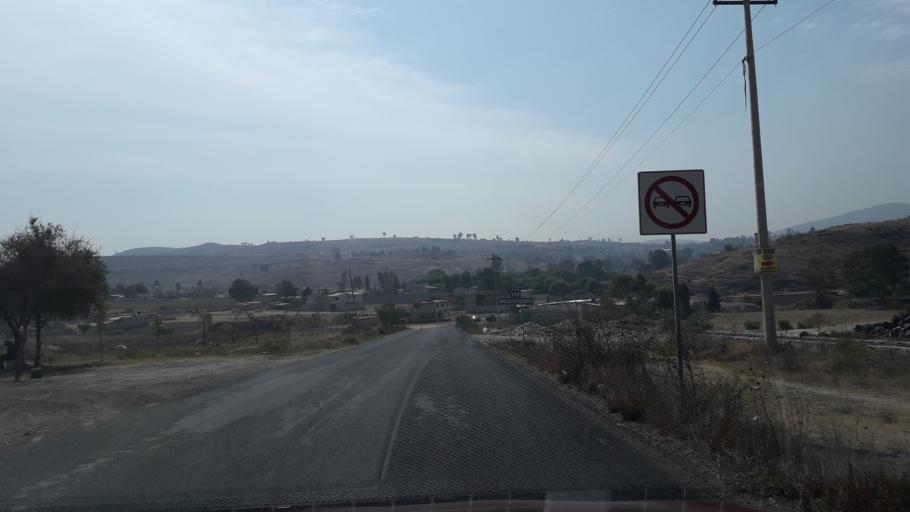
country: MX
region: Puebla
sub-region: Puebla
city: El Capulo (La Quebradora)
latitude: 18.9285
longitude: -98.2568
